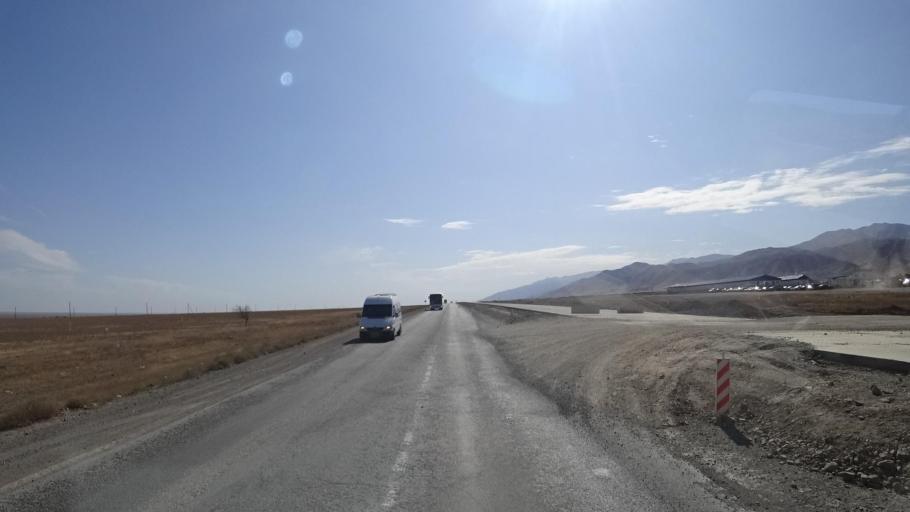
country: KG
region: Chuy
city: Ivanovka
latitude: 43.3907
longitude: 75.1413
